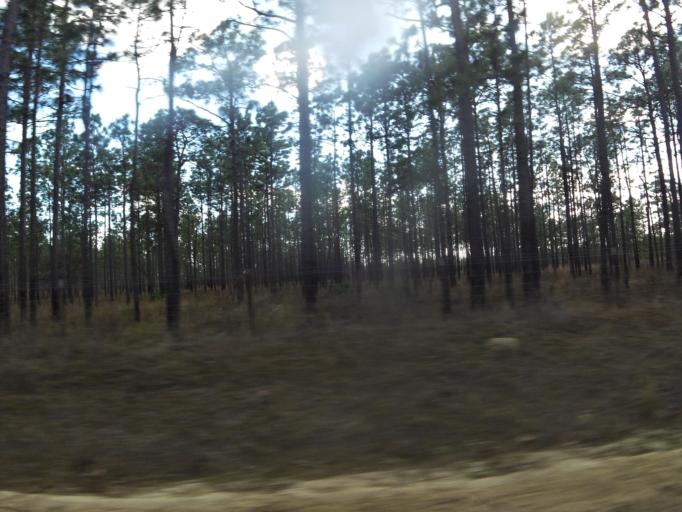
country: US
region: Florida
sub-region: Clay County
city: Keystone Heights
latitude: 29.7866
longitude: -81.8714
